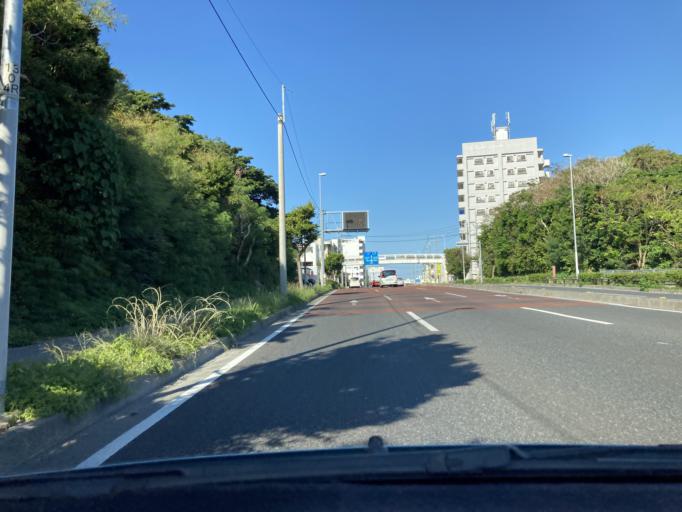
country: JP
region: Okinawa
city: Ginowan
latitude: 26.2536
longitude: 127.7518
